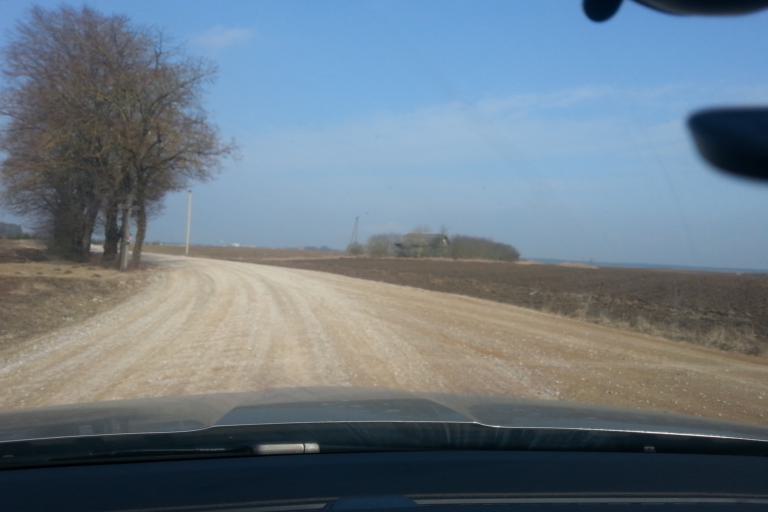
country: LT
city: Trakai
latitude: 54.5851
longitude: 24.9774
